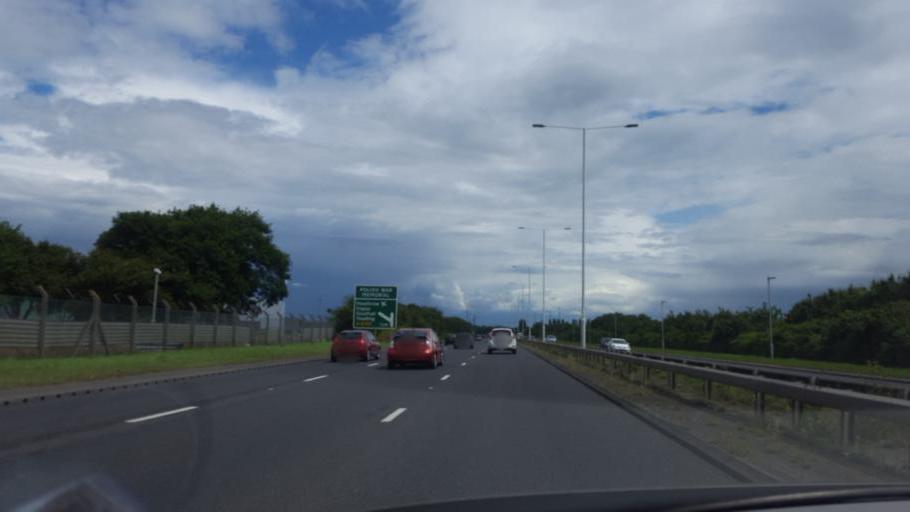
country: GB
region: England
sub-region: Greater London
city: Ruislip
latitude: 51.5484
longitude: -0.4153
